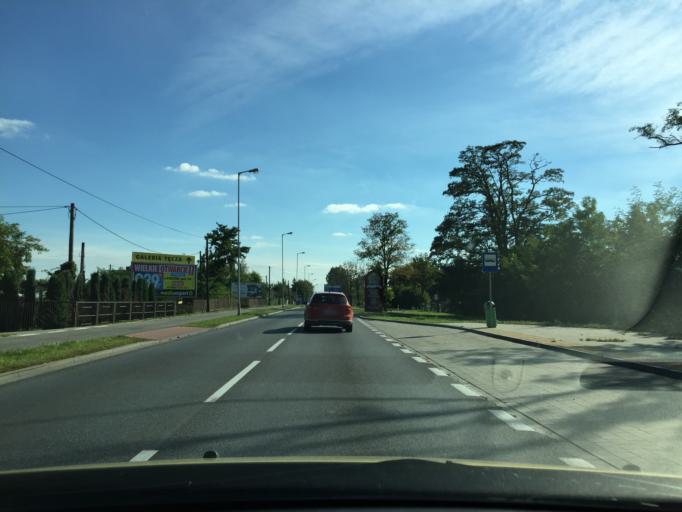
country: PL
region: Greater Poland Voivodeship
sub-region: Kalisz
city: Kalisz
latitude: 51.7885
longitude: 18.0904
